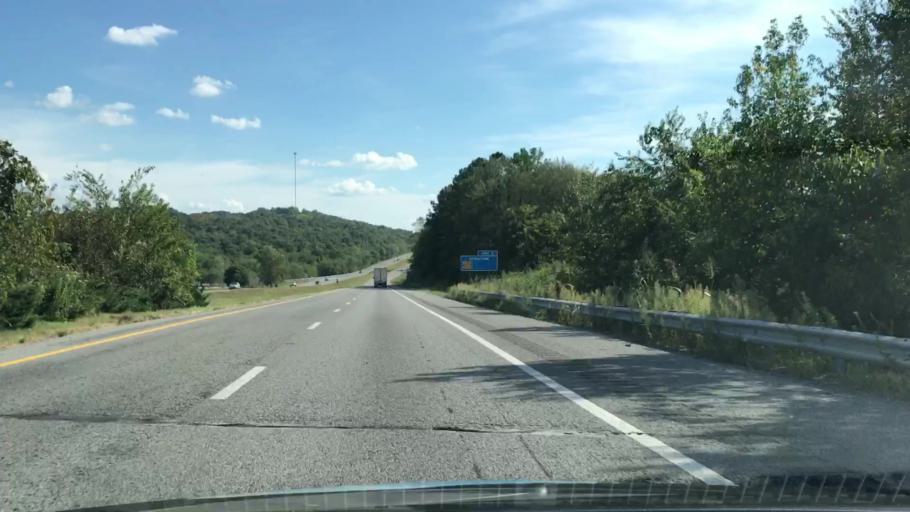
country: US
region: Alabama
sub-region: Limestone County
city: Ardmore
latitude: 35.0382
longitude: -86.8794
